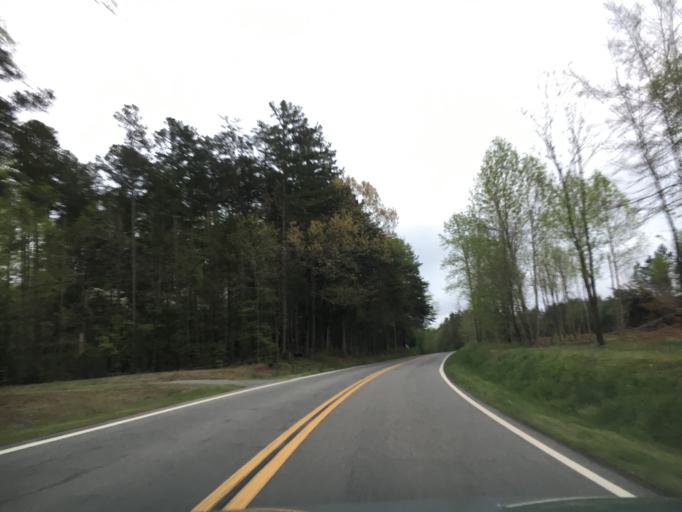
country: US
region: Virginia
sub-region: Halifax County
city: South Boston
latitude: 36.6806
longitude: -78.8951
